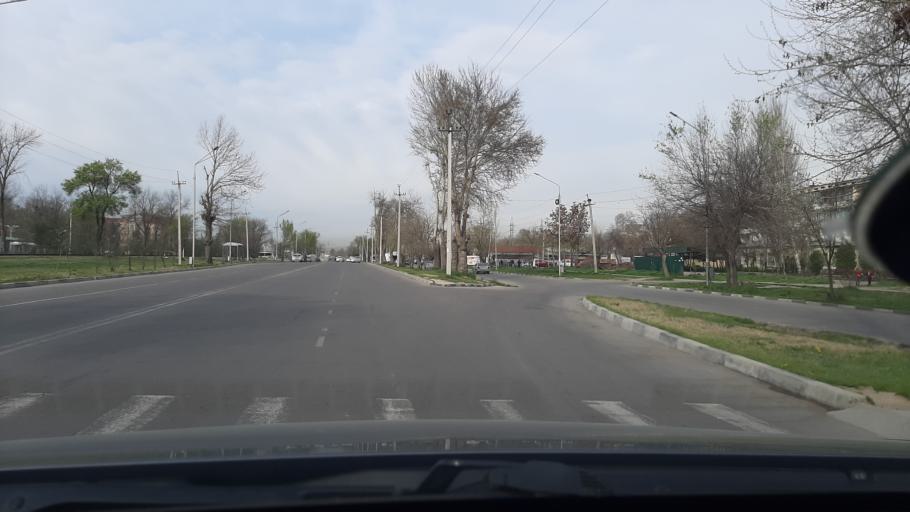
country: TJ
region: Dushanbe
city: Dushanbe
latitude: 38.5688
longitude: 68.7475
